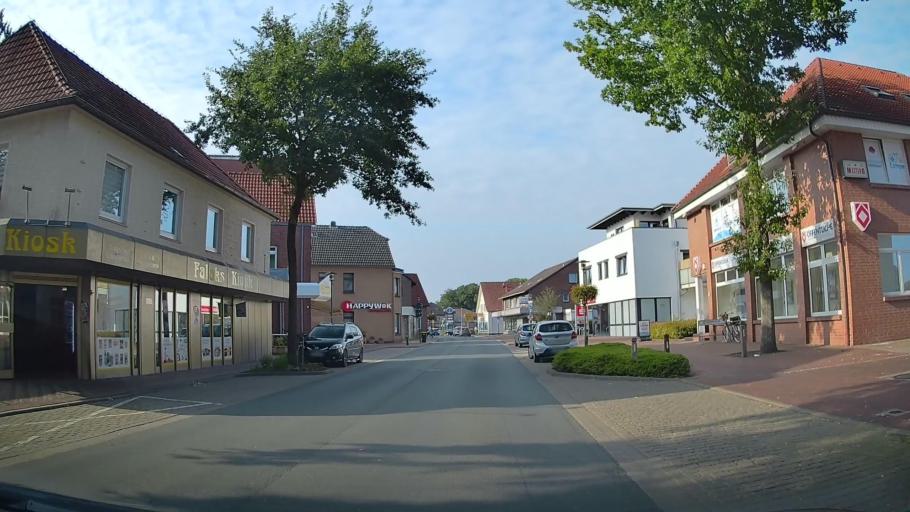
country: DE
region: Lower Saxony
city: Barssel
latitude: 53.1673
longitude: 7.7461
